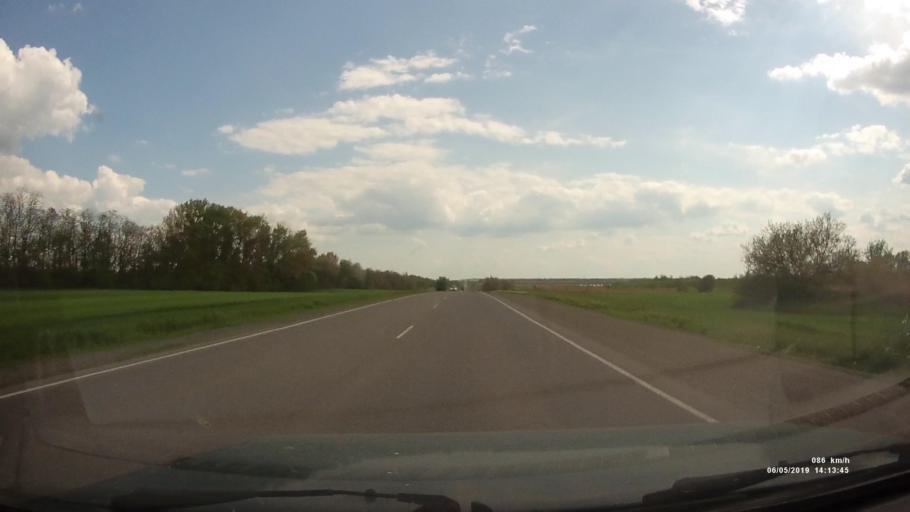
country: RU
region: Rostov
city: Kamenolomni
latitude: 47.6572
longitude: 40.2946
